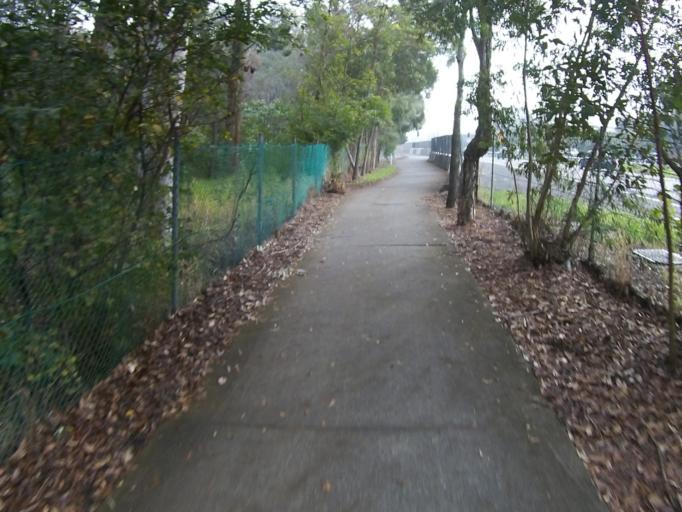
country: AU
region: Queensland
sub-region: Brisbane
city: Nathan
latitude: -27.5486
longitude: 153.0647
